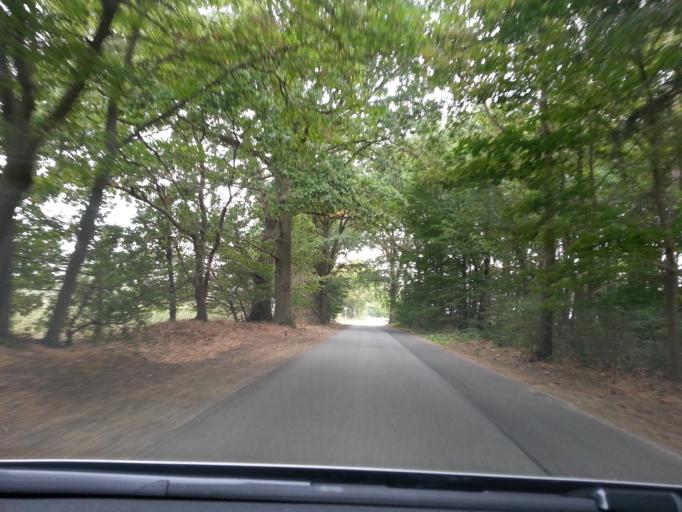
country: DE
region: Mecklenburg-Vorpommern
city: Ferdinandshof
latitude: 53.6577
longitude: 13.9184
